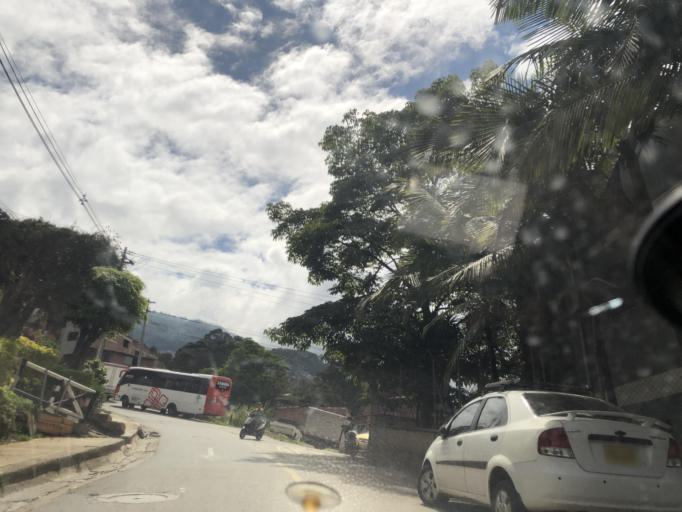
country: CO
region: Antioquia
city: Bello
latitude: 6.3093
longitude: -75.5502
